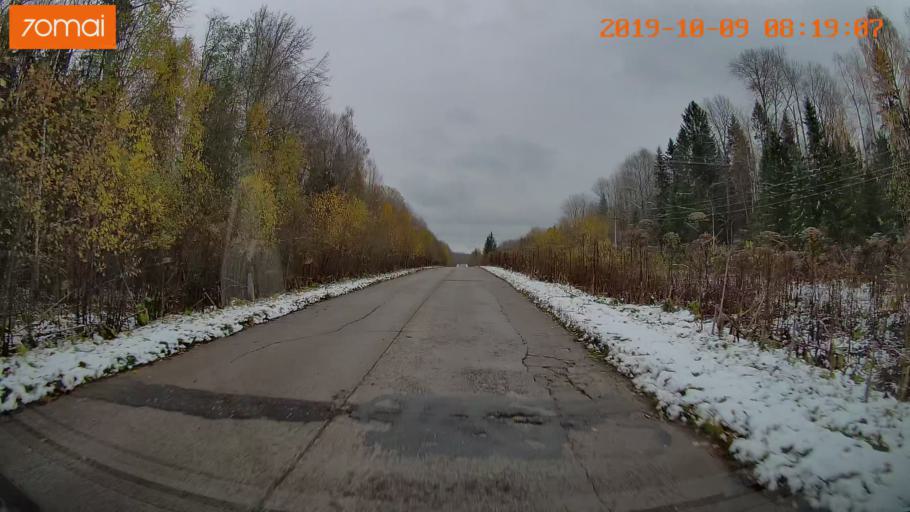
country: RU
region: Vologda
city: Gryazovets
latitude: 58.7414
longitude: 40.2358
